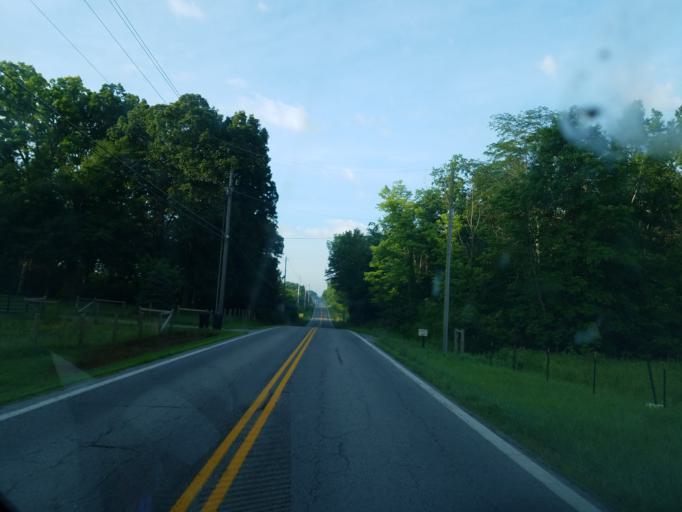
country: US
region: Ohio
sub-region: Marion County
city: Prospect
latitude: 40.4983
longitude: -83.1903
